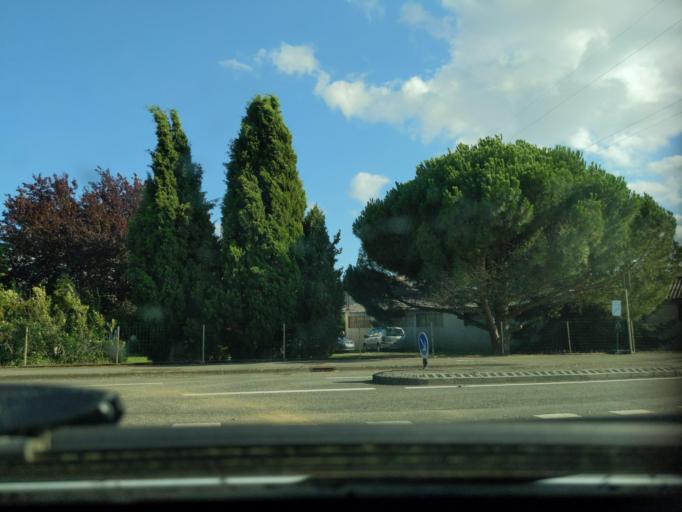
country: FR
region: Midi-Pyrenees
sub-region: Departement de la Haute-Garonne
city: Pibrac
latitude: 43.6099
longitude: 1.2749
